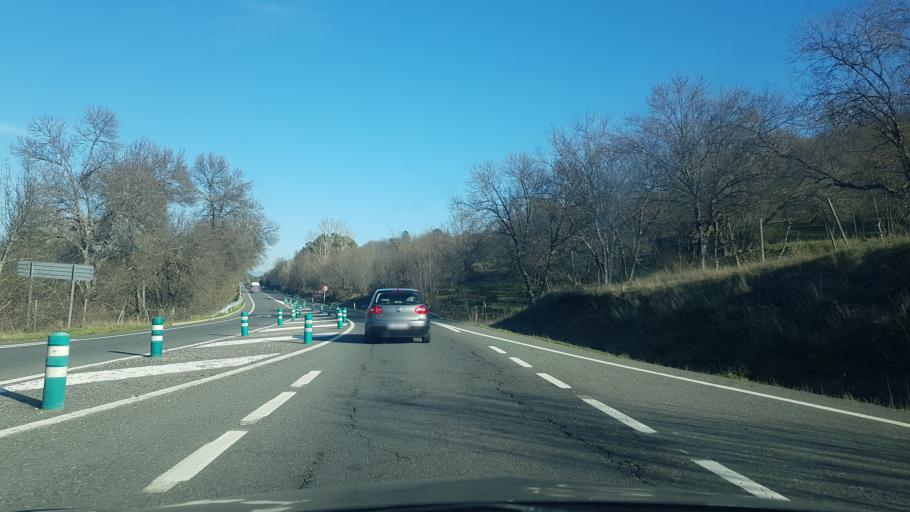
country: ES
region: Madrid
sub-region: Provincia de Madrid
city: Rozas de Puerto Real
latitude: 40.3200
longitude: -4.4899
